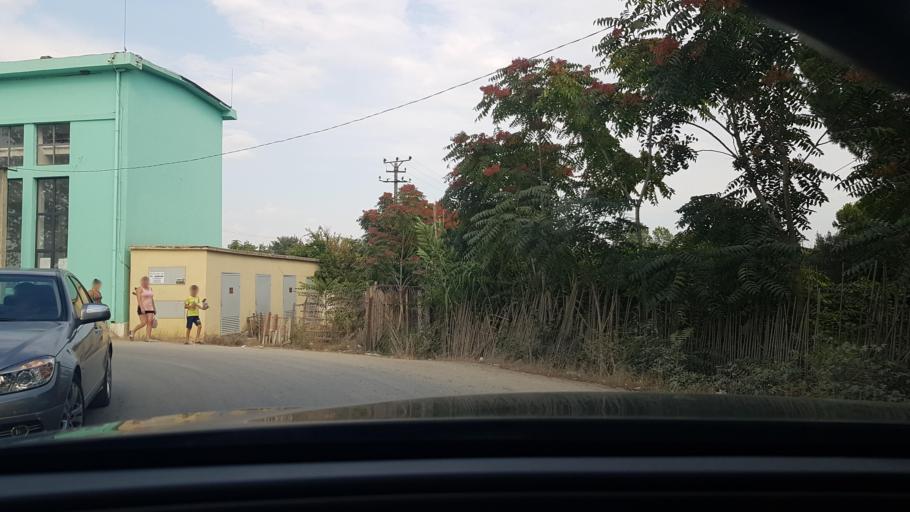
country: AL
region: Durres
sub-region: Rrethi i Durresit
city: Katundi i Ri
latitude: 41.4863
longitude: 19.5173
